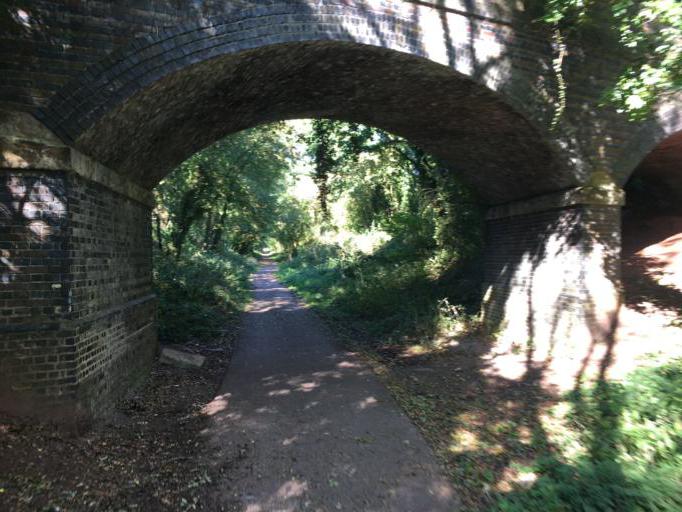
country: GB
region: England
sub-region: Warwickshire
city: Kenilworth
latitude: 52.3624
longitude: -1.5723
